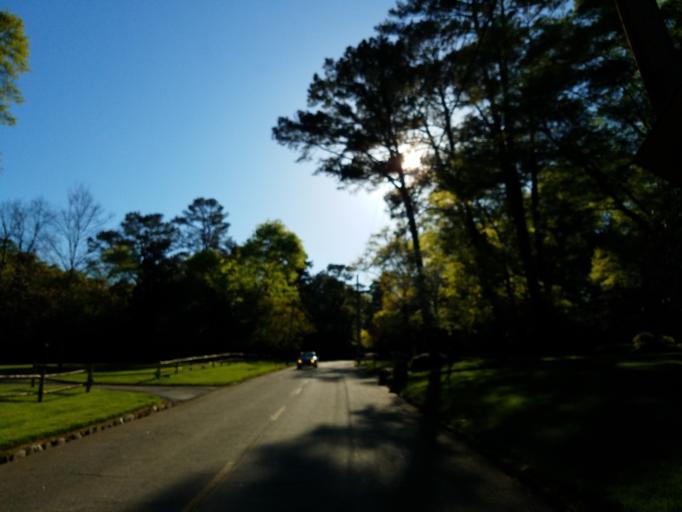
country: US
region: Georgia
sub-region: Cobb County
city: Vinings
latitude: 33.8375
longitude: -84.4440
